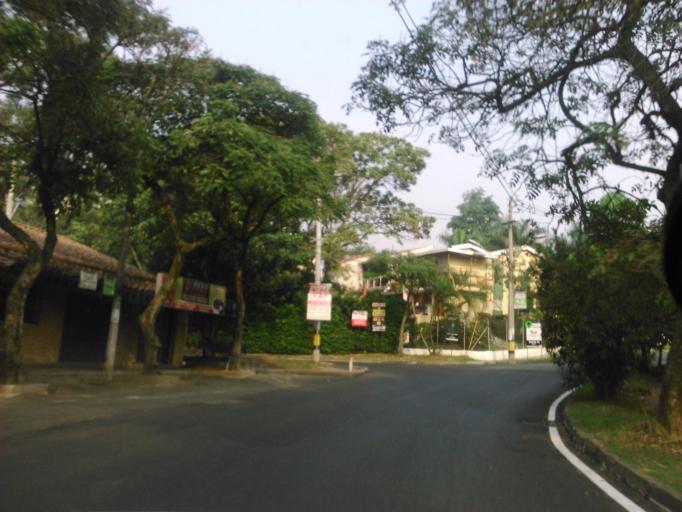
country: CO
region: Antioquia
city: Sabaneta
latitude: 6.1578
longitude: -75.6231
